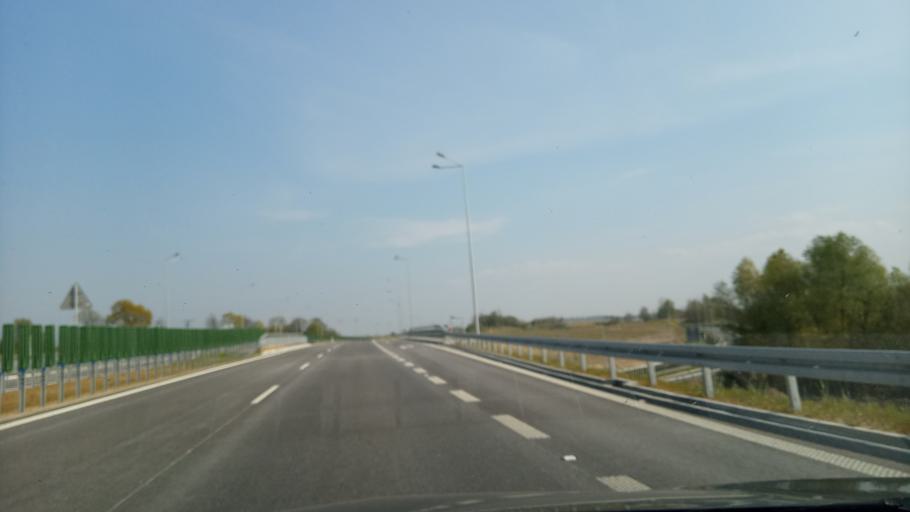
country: PL
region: West Pomeranian Voivodeship
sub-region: Powiat szczecinecki
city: Szczecinek
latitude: 53.7121
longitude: 16.7166
